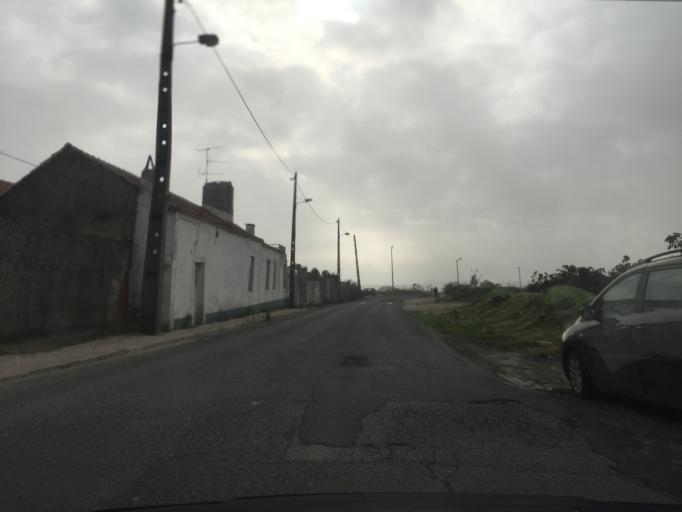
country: PT
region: Lisbon
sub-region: Loures
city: Camarate
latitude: 38.7814
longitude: -9.1412
